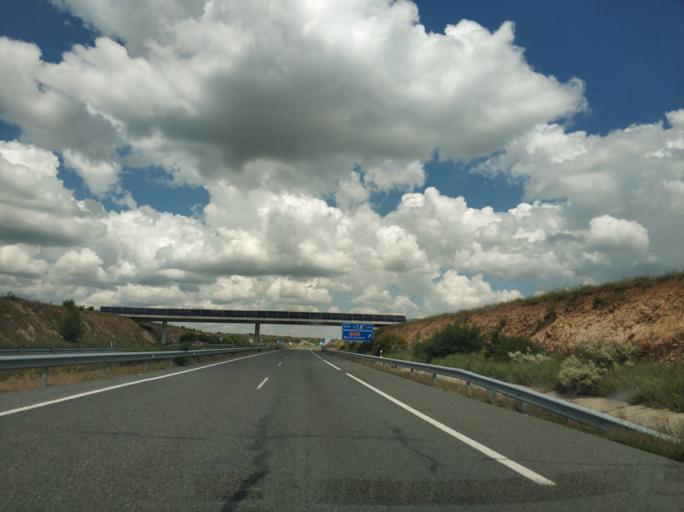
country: ES
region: Castille and Leon
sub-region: Provincia de Salamanca
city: Buenavista
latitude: 40.7898
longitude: -5.6346
